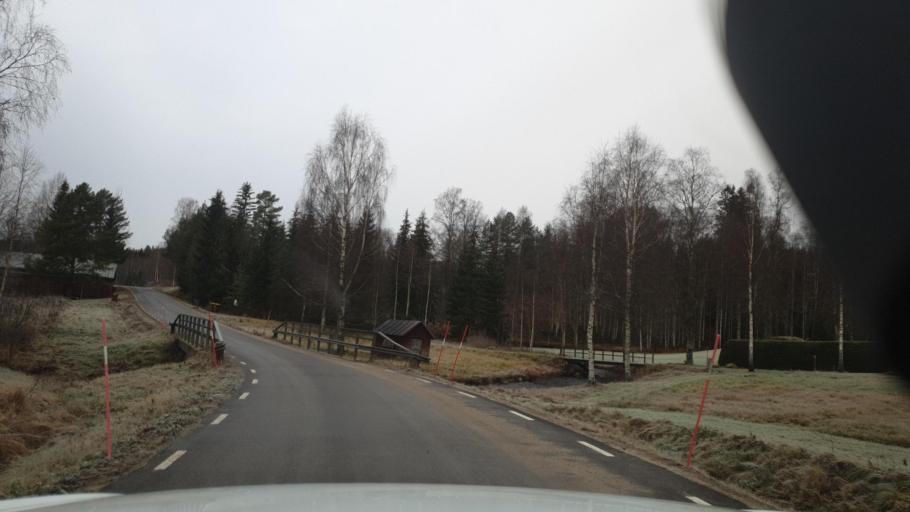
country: SE
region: Vaermland
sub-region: Arvika Kommun
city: Arvika
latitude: 59.7492
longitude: 12.8292
